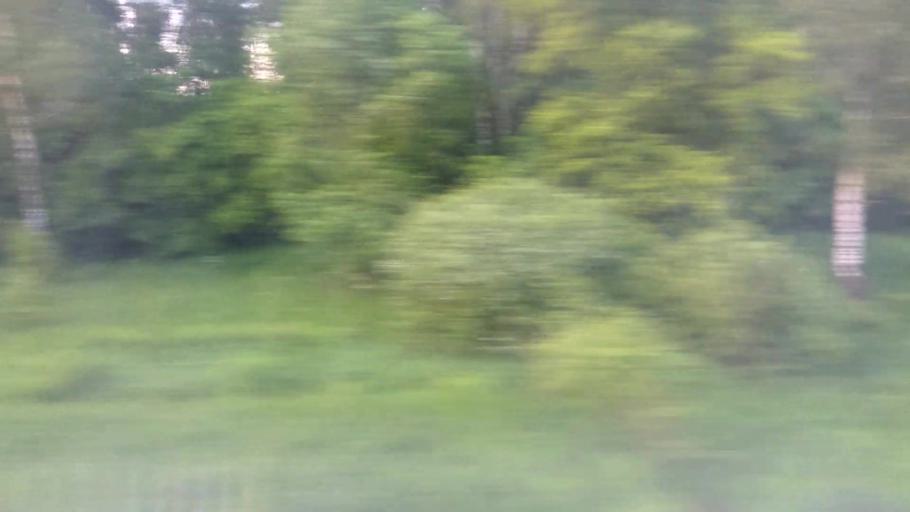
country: RU
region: Moskovskaya
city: Belyye Stolby
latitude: 55.3245
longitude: 37.8585
